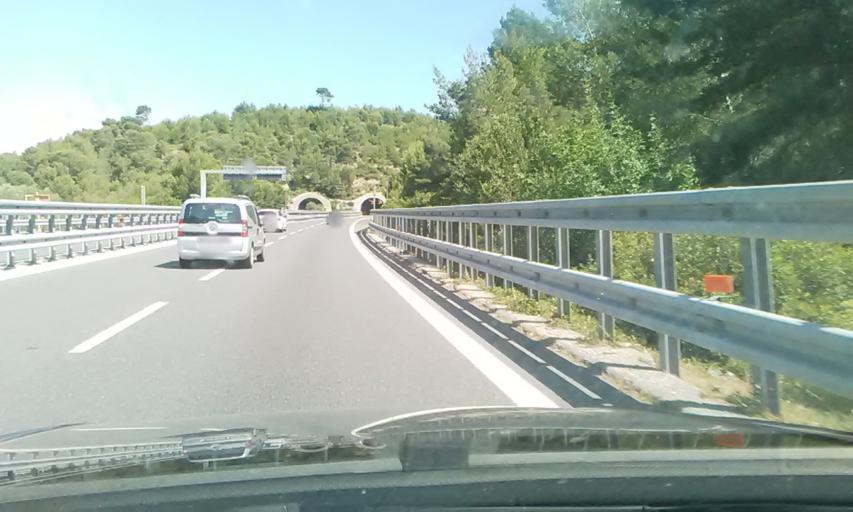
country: IT
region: Liguria
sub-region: Provincia di Savona
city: Laigueglia
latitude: 43.9753
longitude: 8.1412
